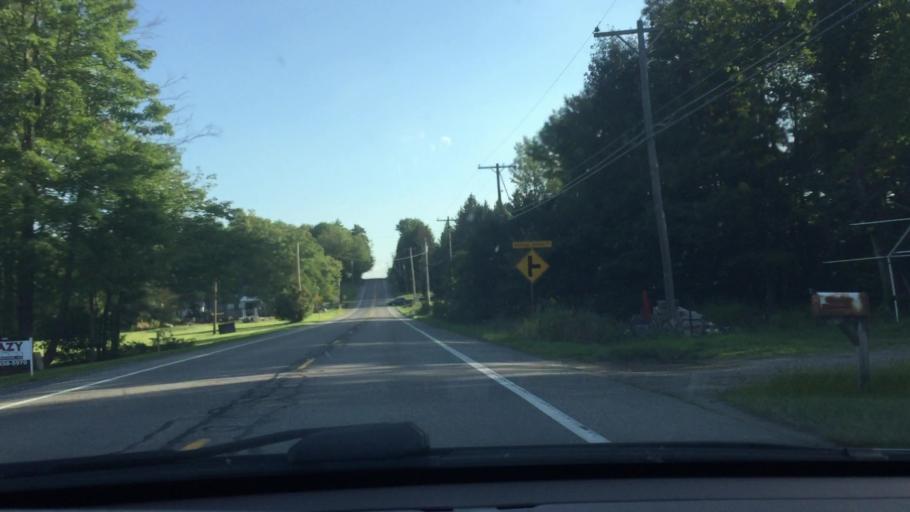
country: US
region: Pennsylvania
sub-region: Mercer County
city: Grove City
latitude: 41.1922
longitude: -80.0816
